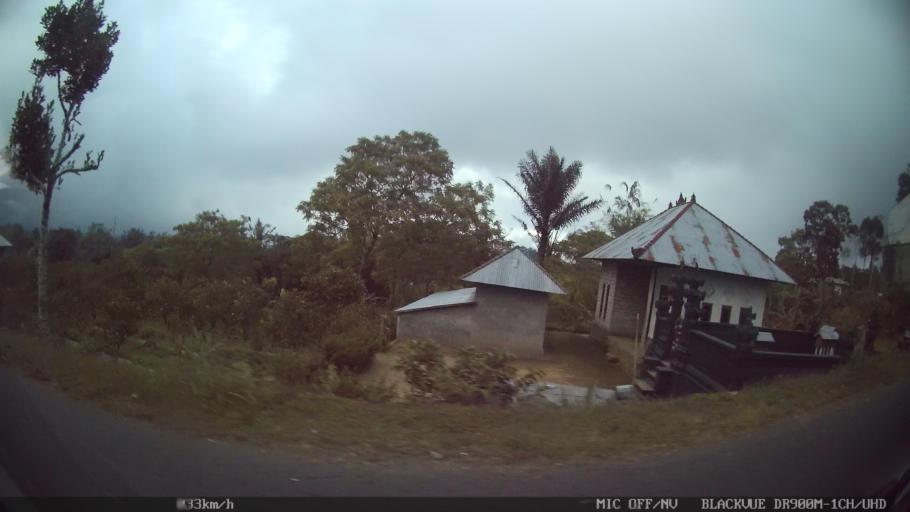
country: ID
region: Bali
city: Banjar Kedisan
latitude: -8.2687
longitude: 115.3306
